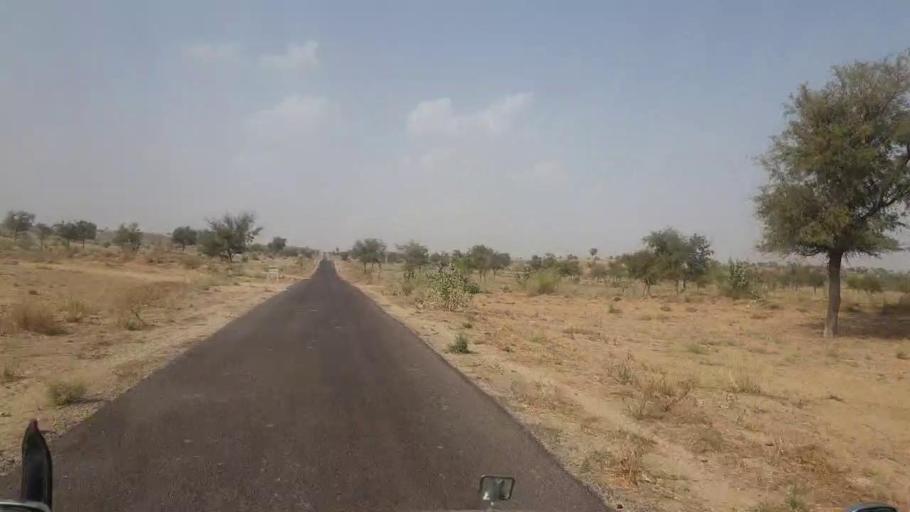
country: PK
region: Sindh
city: Islamkot
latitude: 25.1839
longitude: 70.2865
